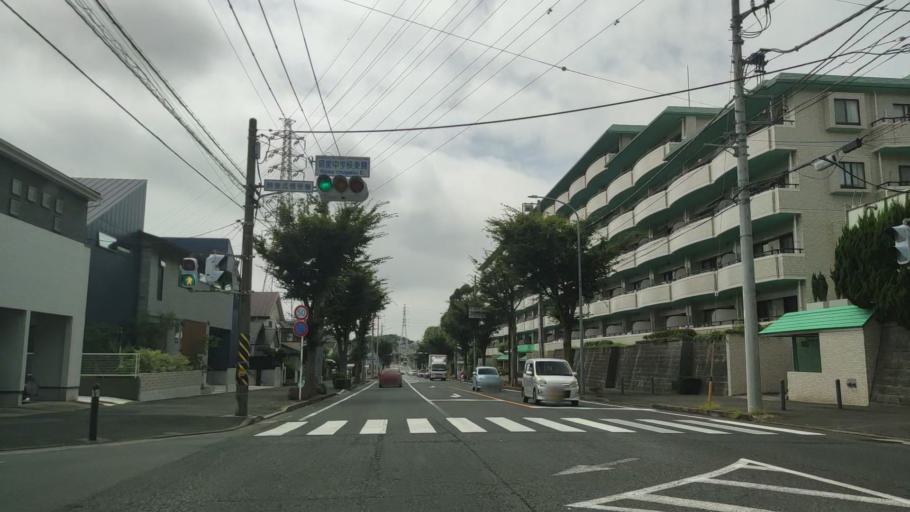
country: JP
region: Kanagawa
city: Fujisawa
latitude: 35.4157
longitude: 139.5226
